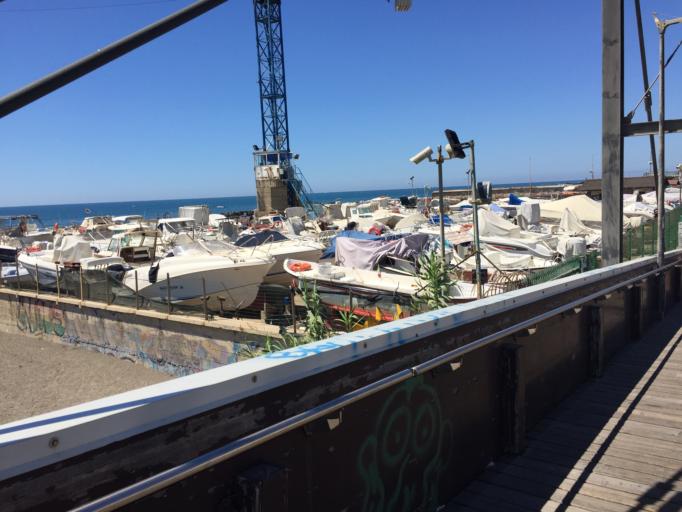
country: IT
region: Latium
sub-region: Citta metropolitana di Roma Capitale
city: Ladispoli
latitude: 41.9496
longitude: 12.0722
